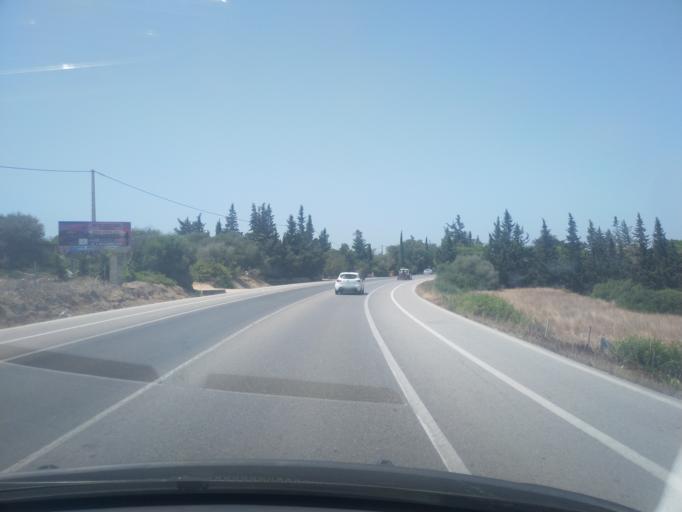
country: ES
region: Andalusia
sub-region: Provincia de Cadiz
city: Chiclana de la Frontera
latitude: 36.3909
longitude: -6.1423
